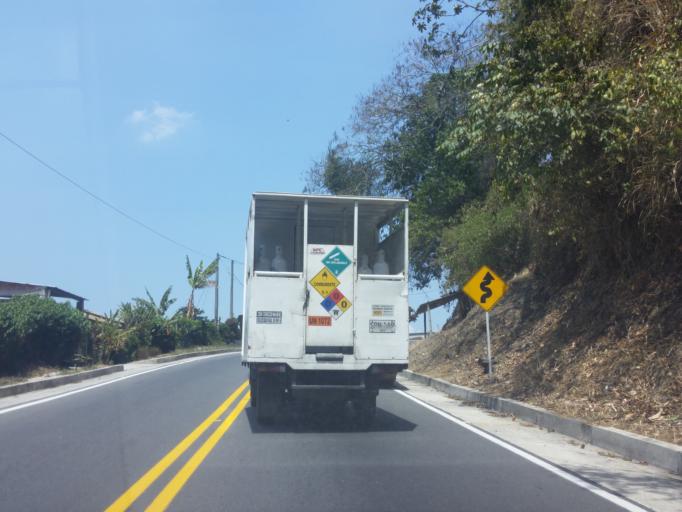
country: CO
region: Caldas
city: Chinchina
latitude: 5.0063
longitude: -75.5678
